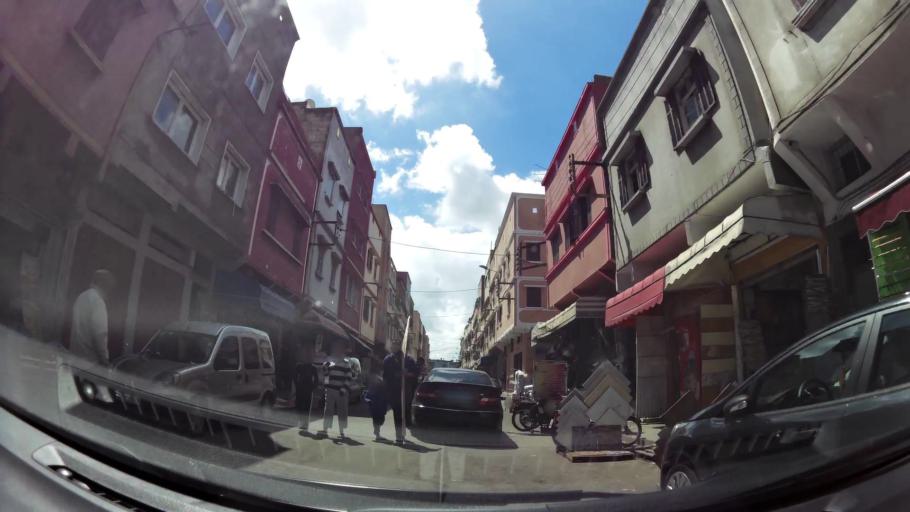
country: MA
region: Grand Casablanca
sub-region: Casablanca
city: Casablanca
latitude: 33.5615
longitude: -7.5998
